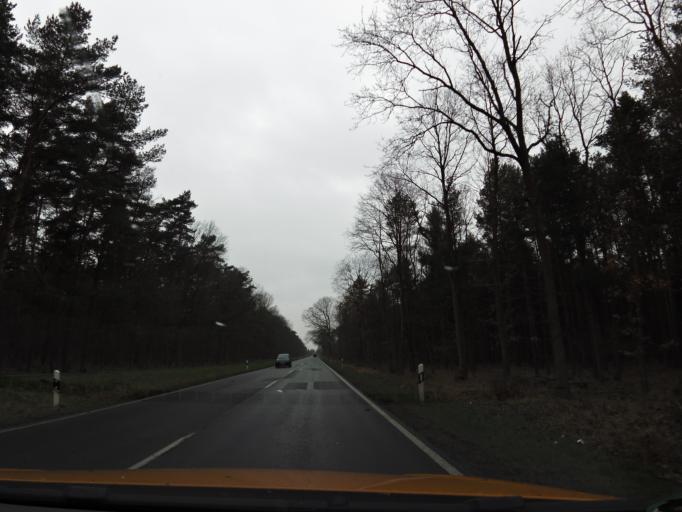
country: DE
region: Brandenburg
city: Gross Kreutz
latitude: 52.4054
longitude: 12.7507
